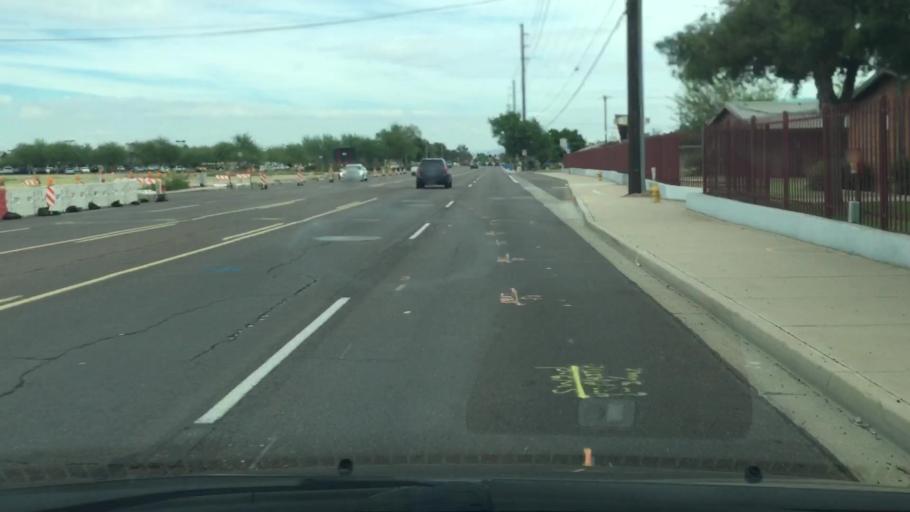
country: US
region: Arizona
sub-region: Maricopa County
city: Phoenix
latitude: 33.3883
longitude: -112.0472
